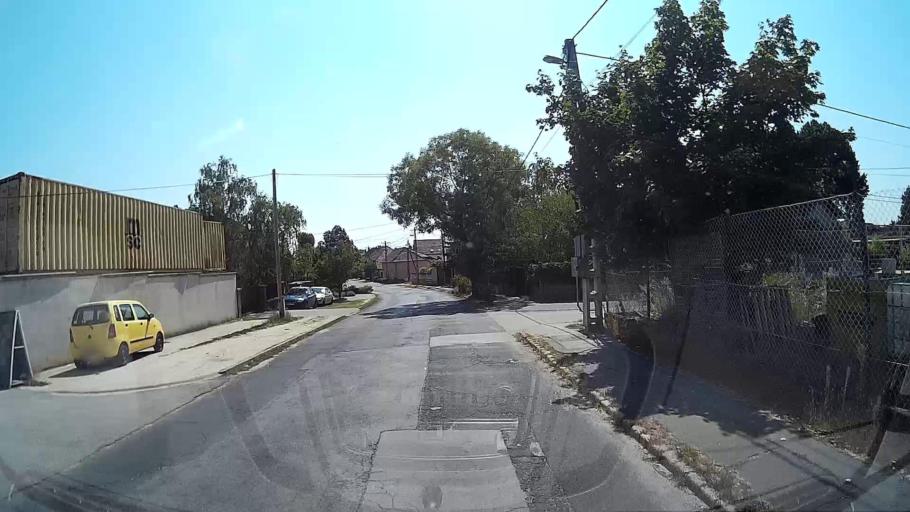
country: HU
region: Budapest
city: Budapest XXIII. keruelet
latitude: 47.4129
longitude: 19.1184
